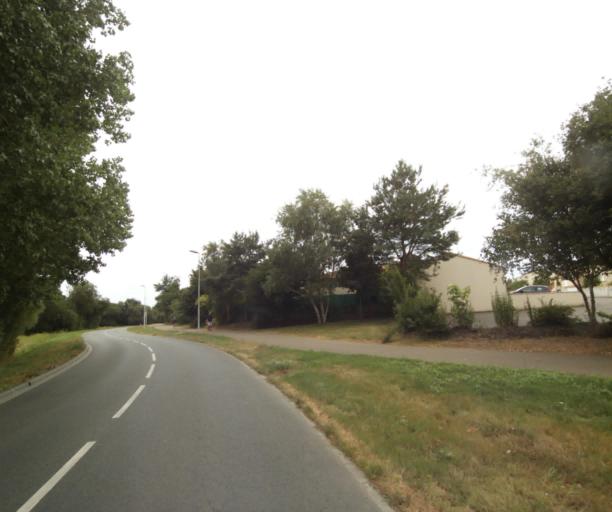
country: FR
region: Pays de la Loire
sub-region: Departement de la Vendee
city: Chateau-d'Olonne
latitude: 46.4994
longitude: -1.7412
